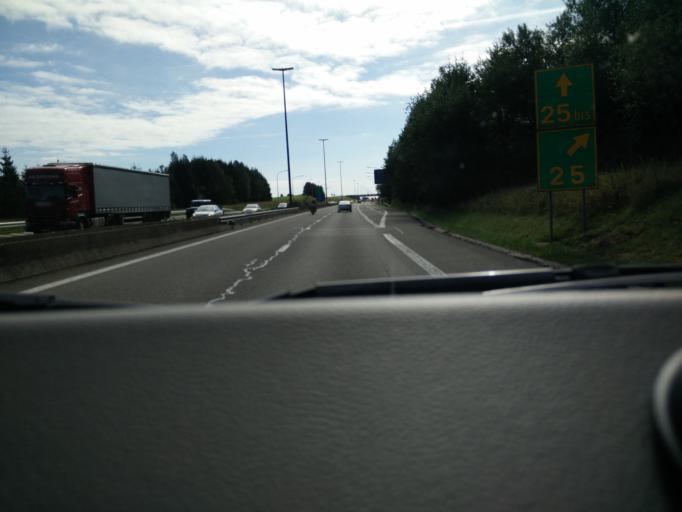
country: BE
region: Wallonia
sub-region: Province du Luxembourg
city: Bertrix
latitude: 49.9061
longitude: 5.3166
